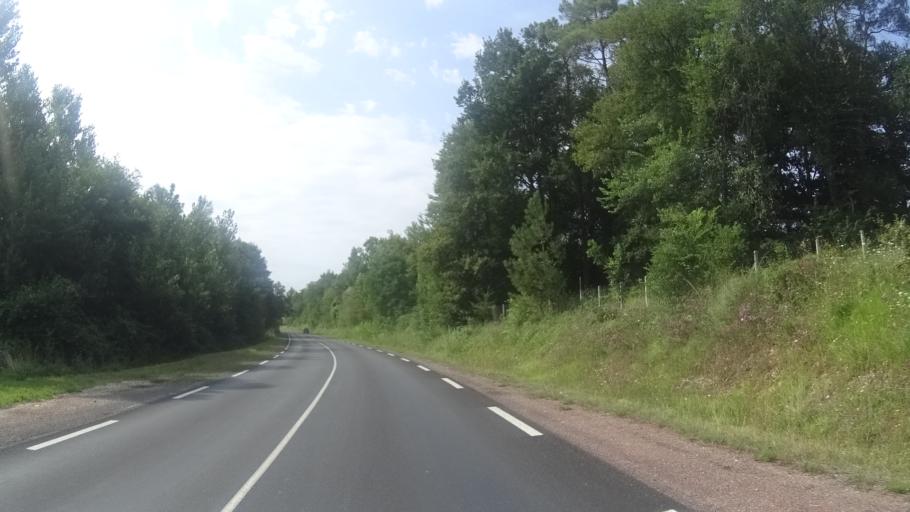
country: FR
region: Aquitaine
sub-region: Departement de la Dordogne
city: Sourzac
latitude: 45.0888
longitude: 0.3815
